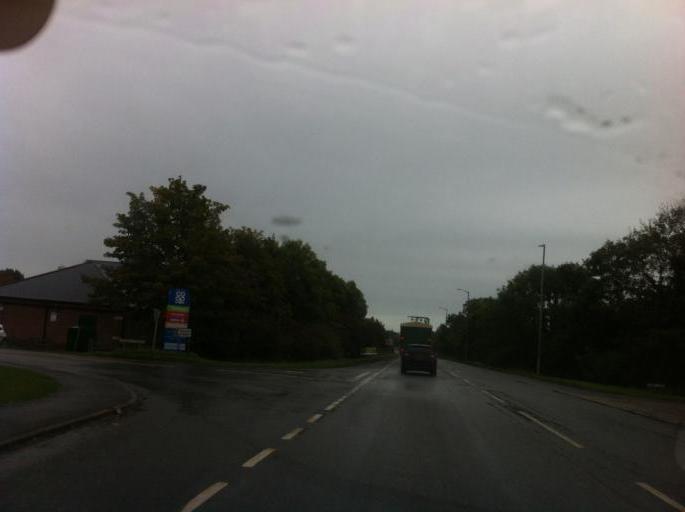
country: GB
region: England
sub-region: Lincolnshire
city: Boston
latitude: 53.0282
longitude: 0.0988
